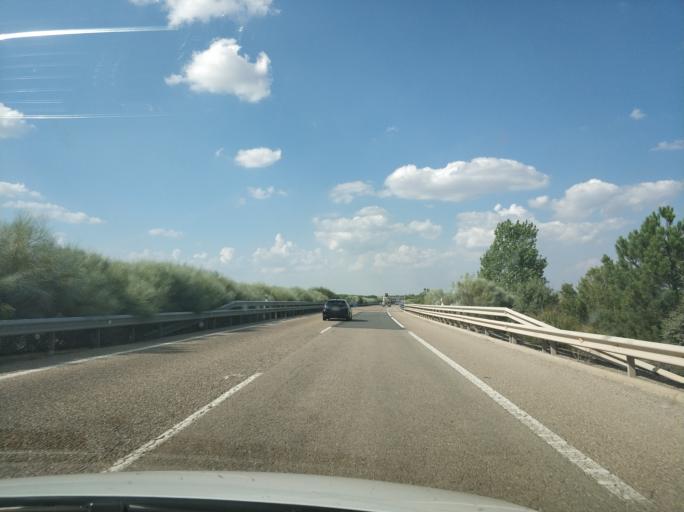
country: ES
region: Castille and Leon
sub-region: Provincia de Zamora
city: Matilla de Arzon
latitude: 42.1096
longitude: -5.6597
